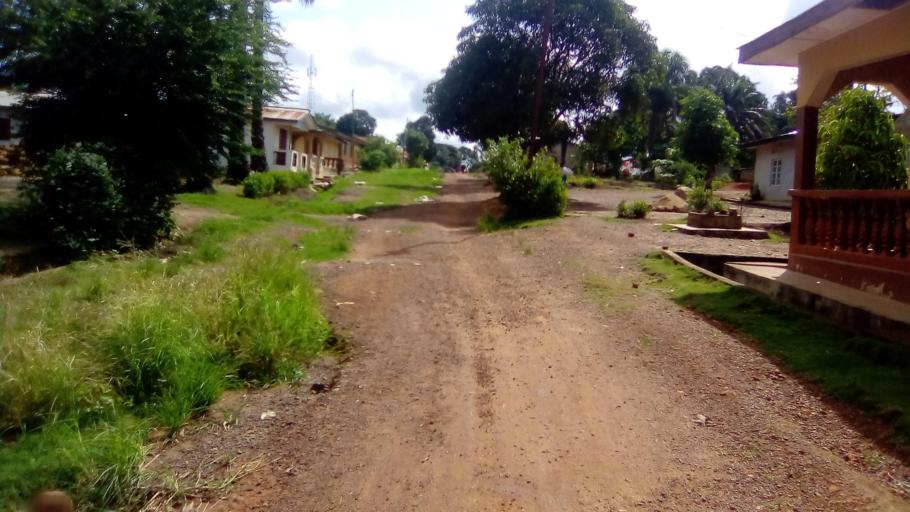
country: SL
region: Southern Province
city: Bo
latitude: 7.9771
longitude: -11.7274
